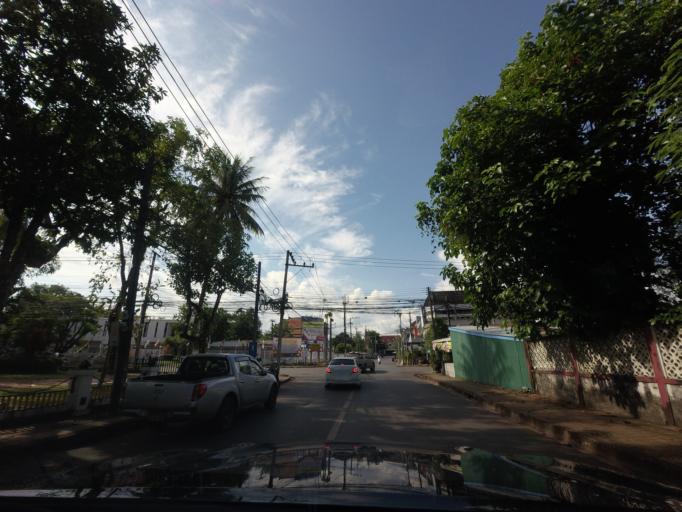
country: TH
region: Nong Khai
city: Nong Khai
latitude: 17.8825
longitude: 102.7437
